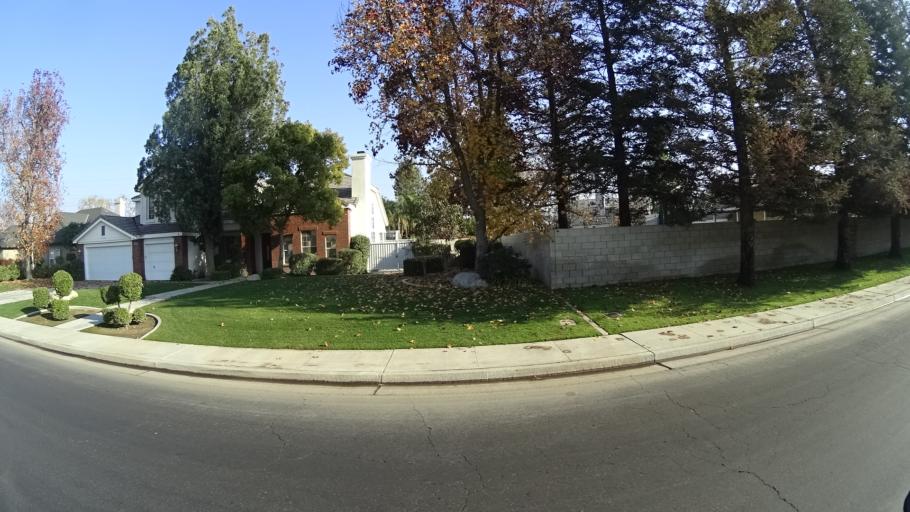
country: US
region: California
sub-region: Kern County
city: Greenacres
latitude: 35.3326
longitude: -119.0979
